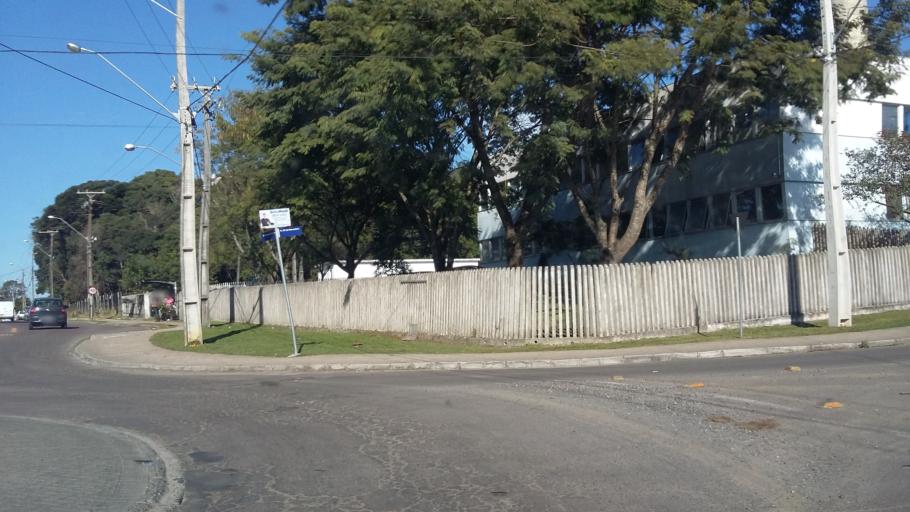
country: BR
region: Parana
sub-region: Campo Largo
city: Campo Largo
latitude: -25.4541
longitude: -49.5415
